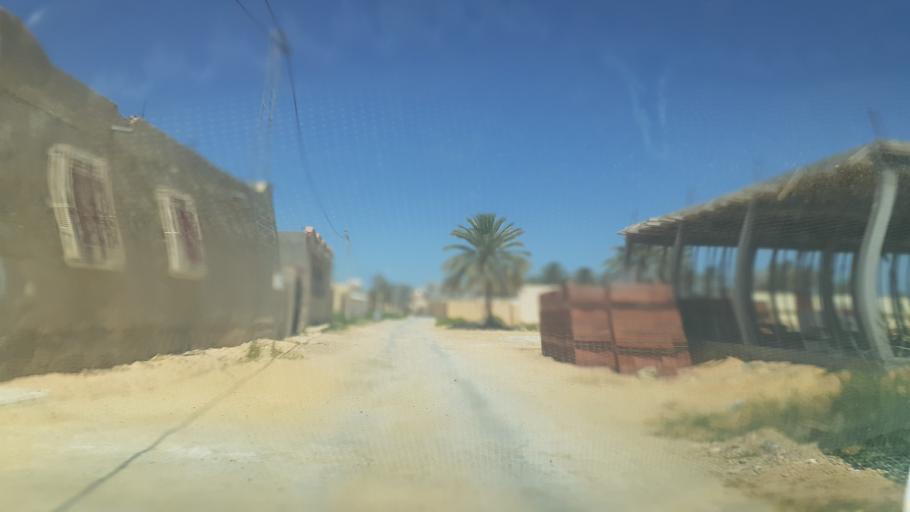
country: TN
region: Qabis
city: Gabes
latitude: 33.9355
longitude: 10.0577
